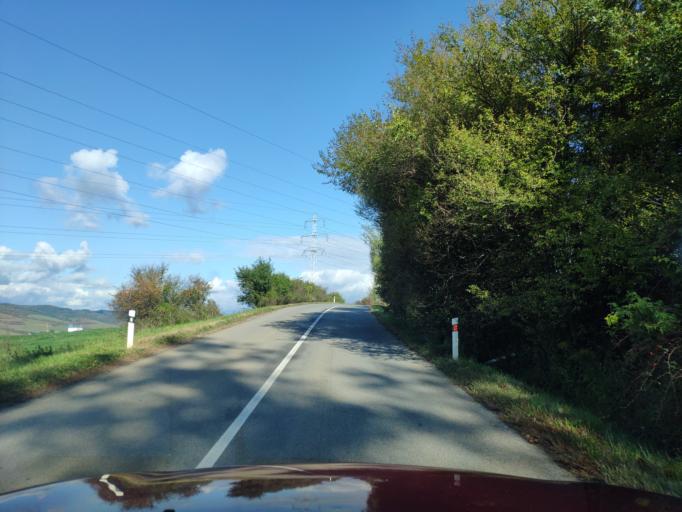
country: SK
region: Presovsky
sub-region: Okres Presov
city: Presov
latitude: 48.9034
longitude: 21.2620
